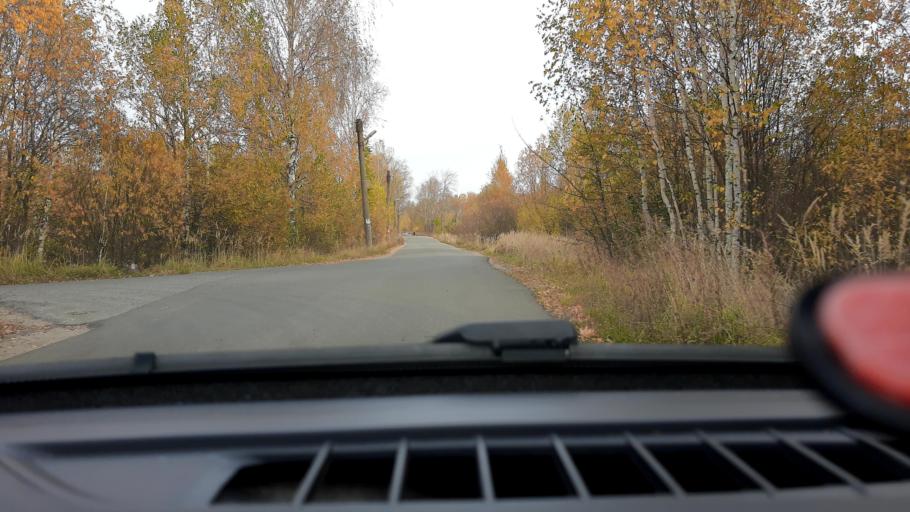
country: RU
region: Nizjnij Novgorod
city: Gorbatovka
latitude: 56.2908
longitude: 43.8315
